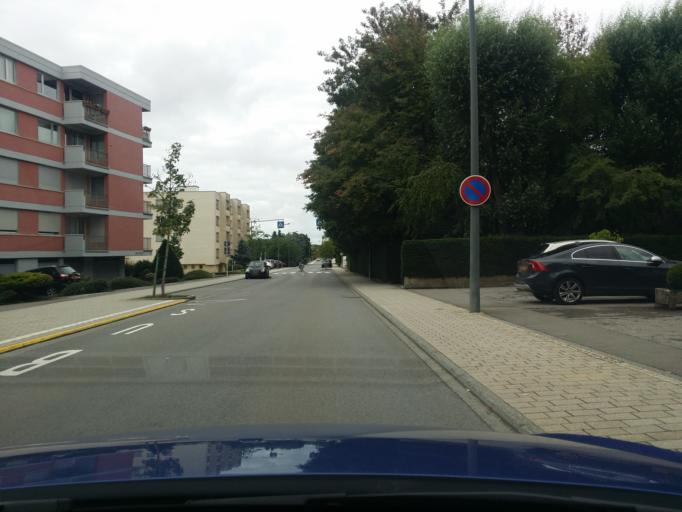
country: LU
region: Luxembourg
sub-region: Canton de Luxembourg
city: Strassen
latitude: 49.6160
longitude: 6.0904
